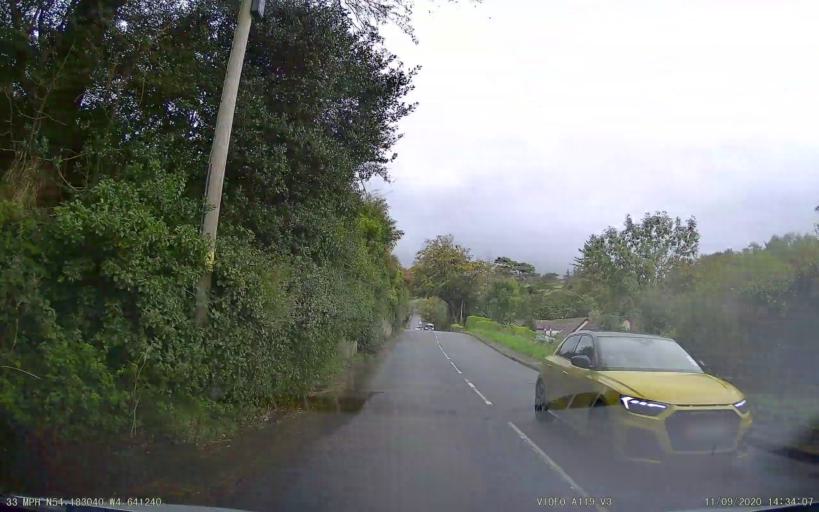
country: IM
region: Castletown
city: Castletown
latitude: 54.1830
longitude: -4.6412
